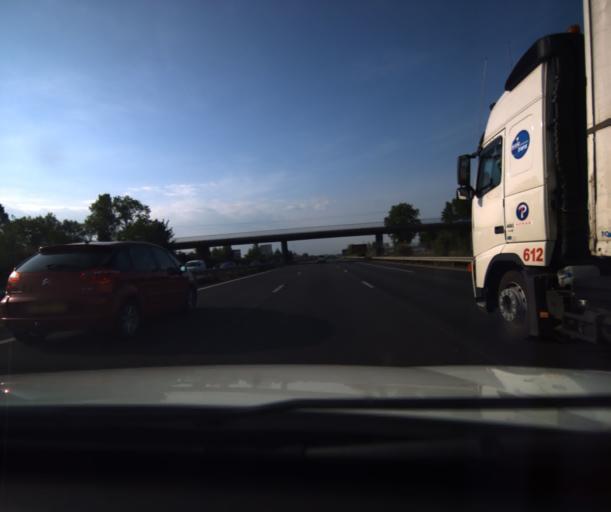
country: FR
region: Midi-Pyrenees
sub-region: Departement de la Haute-Garonne
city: Saint-Alban
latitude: 43.7038
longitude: 1.4061
